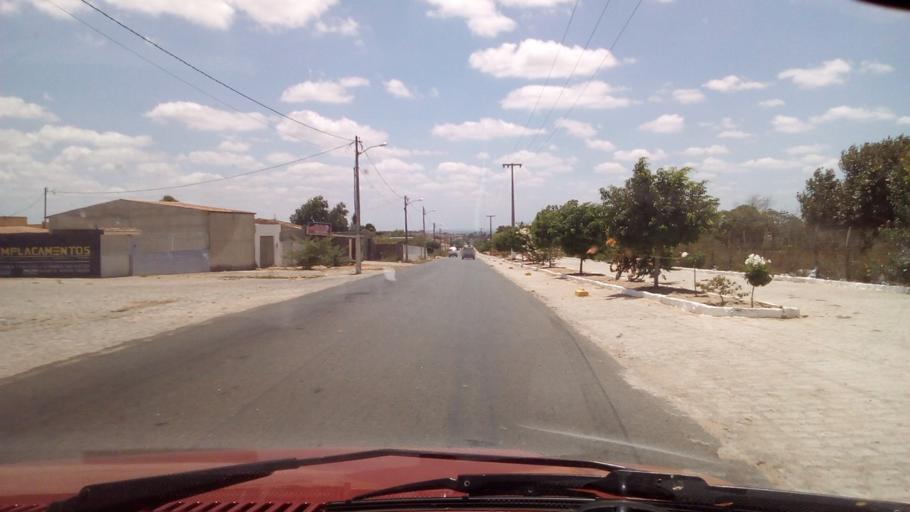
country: BR
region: Paraiba
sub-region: Cacimba De Dentro
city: Cacimba de Dentro
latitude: -6.6286
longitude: -35.7988
